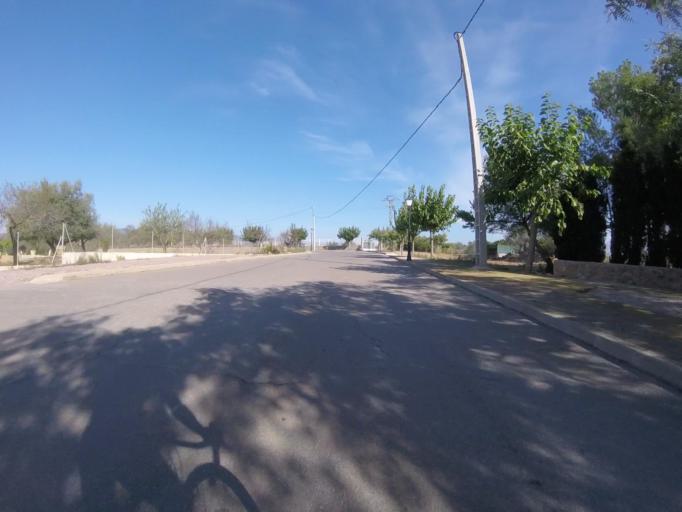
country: ES
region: Valencia
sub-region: Provincia de Castello
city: Benlloch
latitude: 40.2337
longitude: 0.0766
